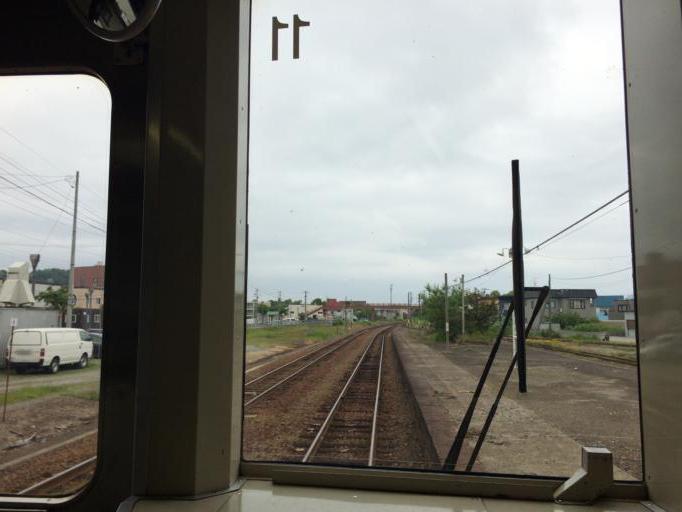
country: JP
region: Hokkaido
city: Yoichi
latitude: 43.1871
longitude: 140.7948
